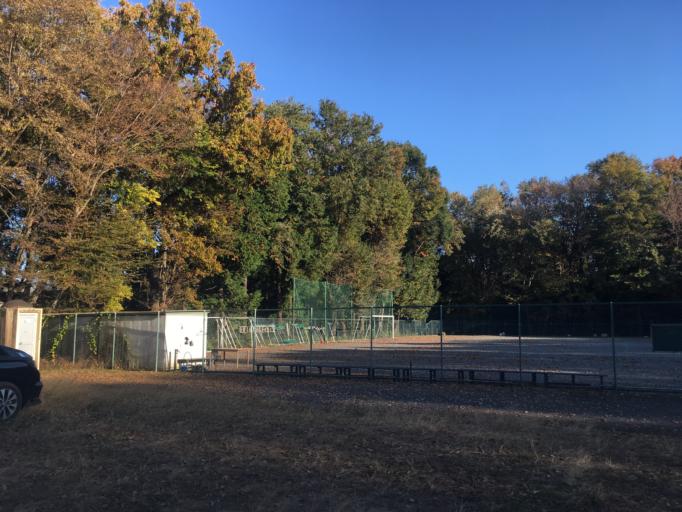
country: JP
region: Saitama
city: Tokorozawa
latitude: 35.8037
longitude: 139.4955
